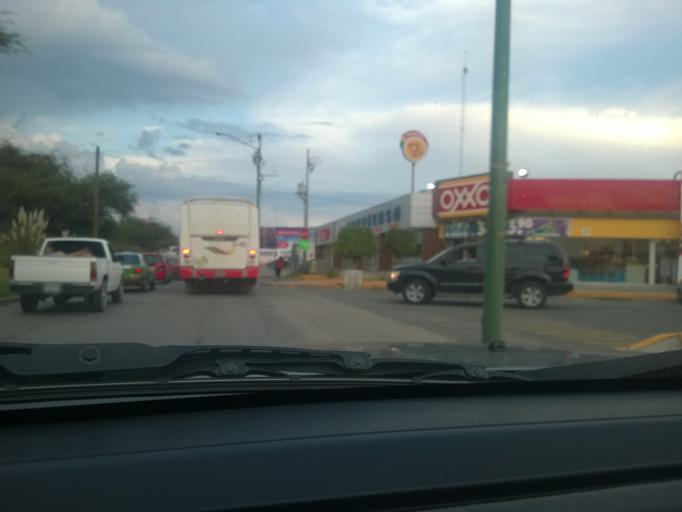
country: MX
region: Guanajuato
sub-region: Leon
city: Fraccionamiento Paraiso Real
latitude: 21.1104
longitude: -101.6016
